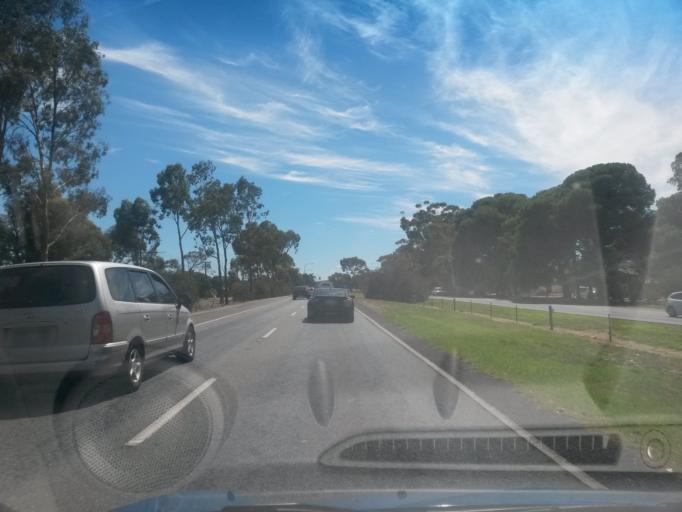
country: AU
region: South Australia
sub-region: Salisbury
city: Salisbury
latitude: -34.7768
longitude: 138.6600
